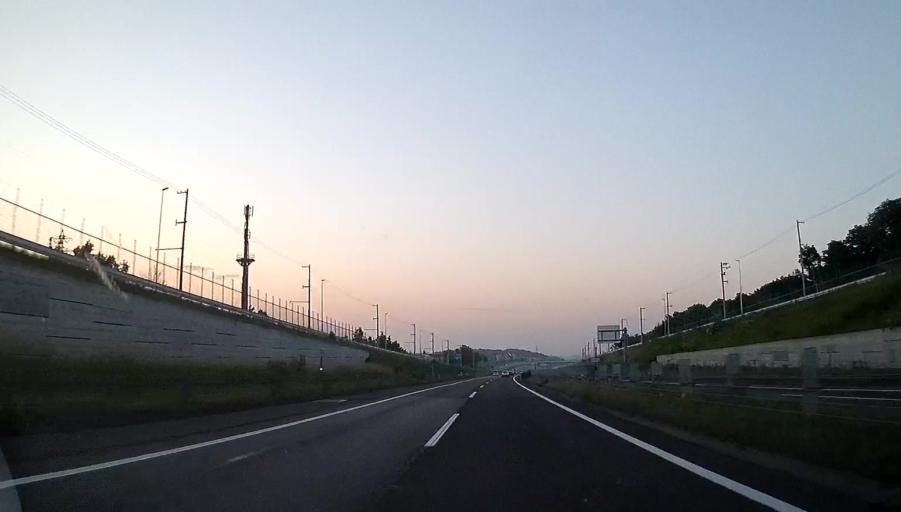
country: JP
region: Hokkaido
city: Kitahiroshima
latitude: 42.9856
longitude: 141.4713
